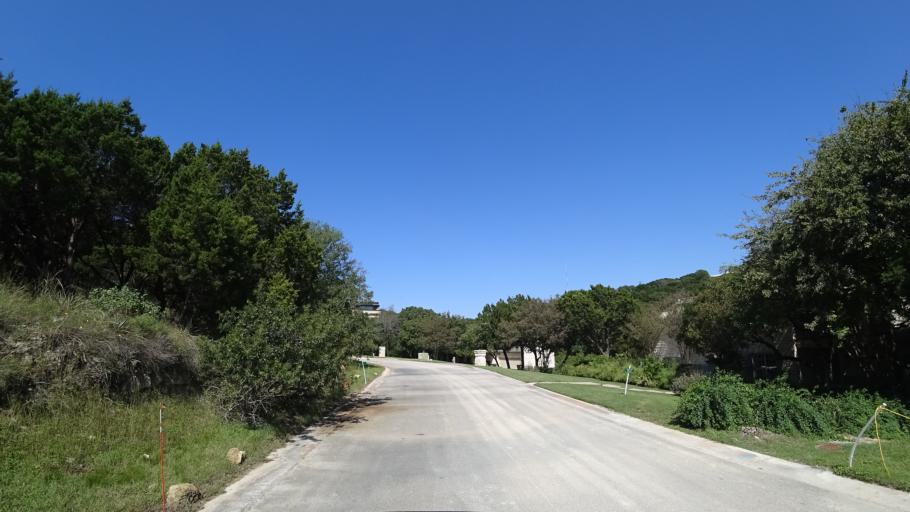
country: US
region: Texas
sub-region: Travis County
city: West Lake Hills
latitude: 30.2958
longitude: -97.8033
